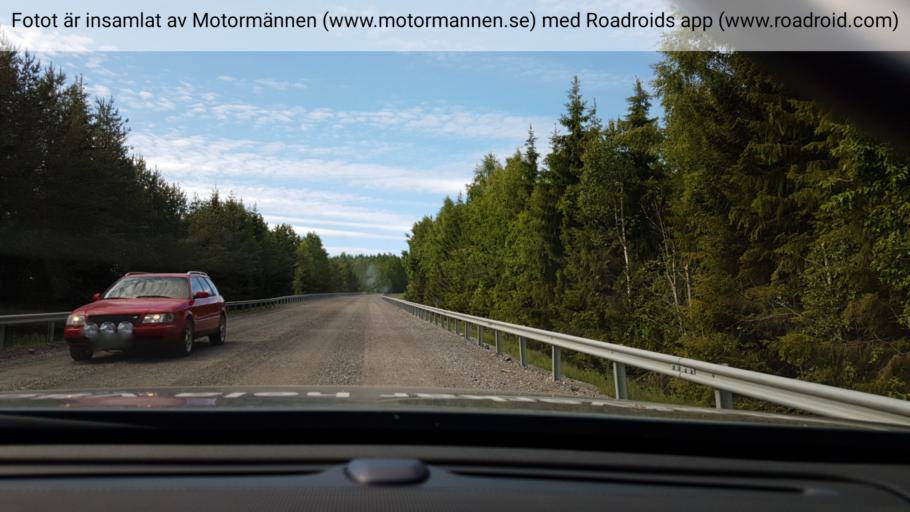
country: SE
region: Vaesterbotten
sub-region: Bjurholms Kommun
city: Bjurholm
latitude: 63.9230
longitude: 19.1853
